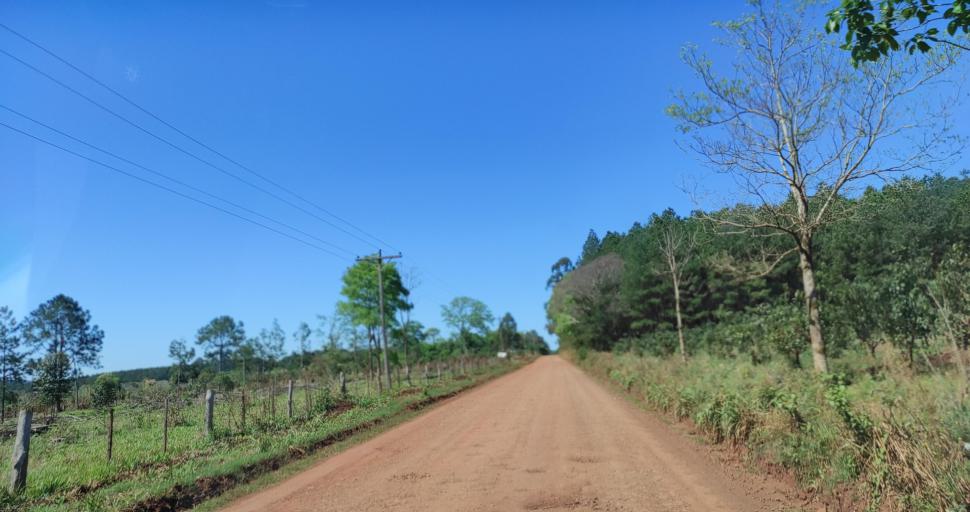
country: AR
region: Misiones
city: Capiovi
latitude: -26.9351
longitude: -55.0332
